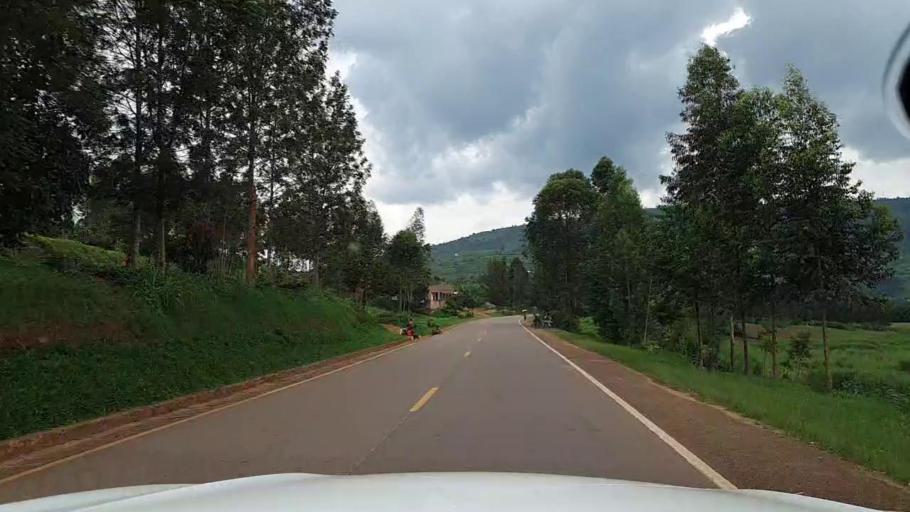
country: RW
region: Kigali
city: Kigali
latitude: -1.7846
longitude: 30.1296
